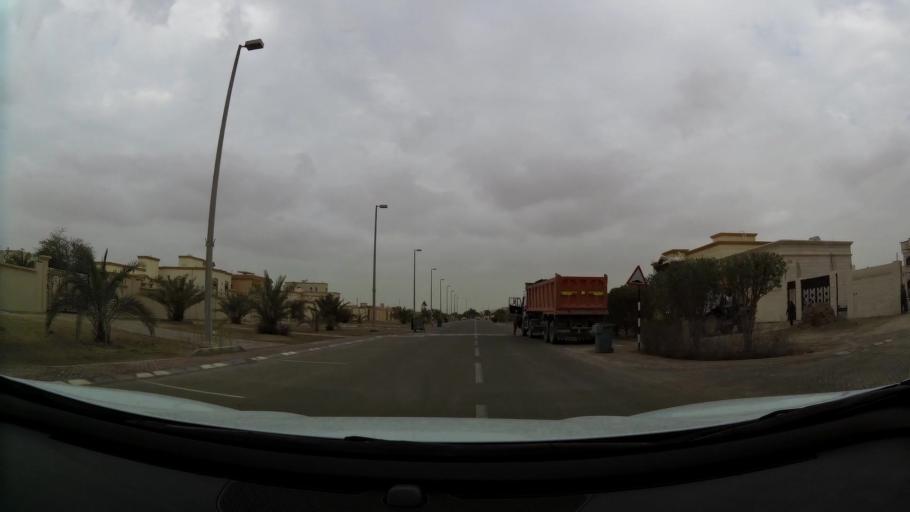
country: AE
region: Abu Dhabi
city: Abu Dhabi
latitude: 24.3558
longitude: 54.6590
